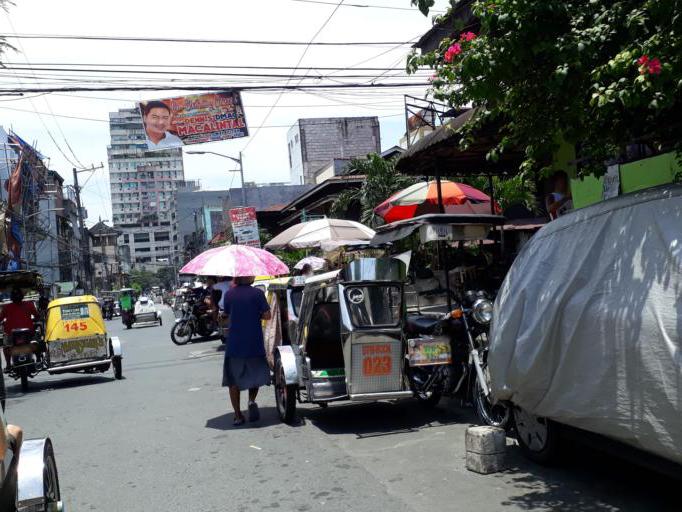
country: PH
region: Calabarzon
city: Del Monte
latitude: 14.6459
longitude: 120.9869
